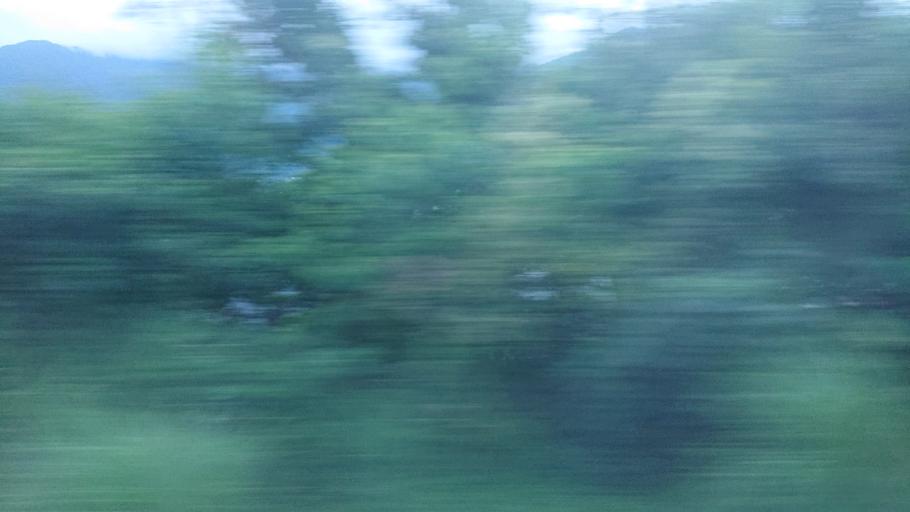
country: TW
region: Taiwan
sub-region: Taitung
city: Taitung
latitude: 23.0425
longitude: 121.1634
